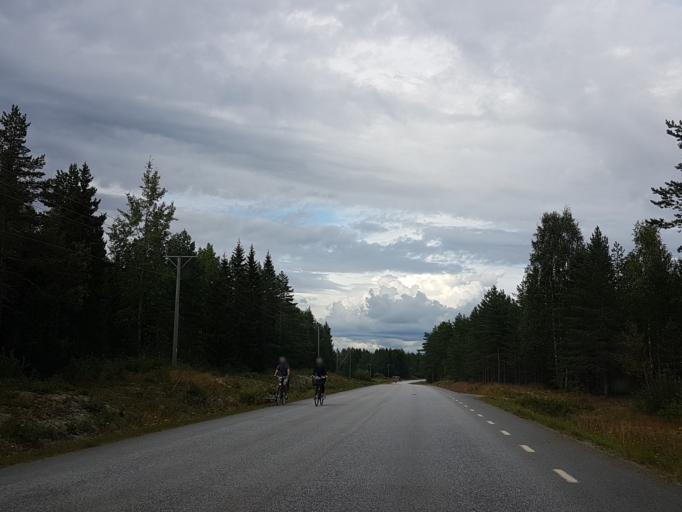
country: SE
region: Vaesterbotten
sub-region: Umea Kommun
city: Taftea
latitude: 63.8254
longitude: 20.4566
